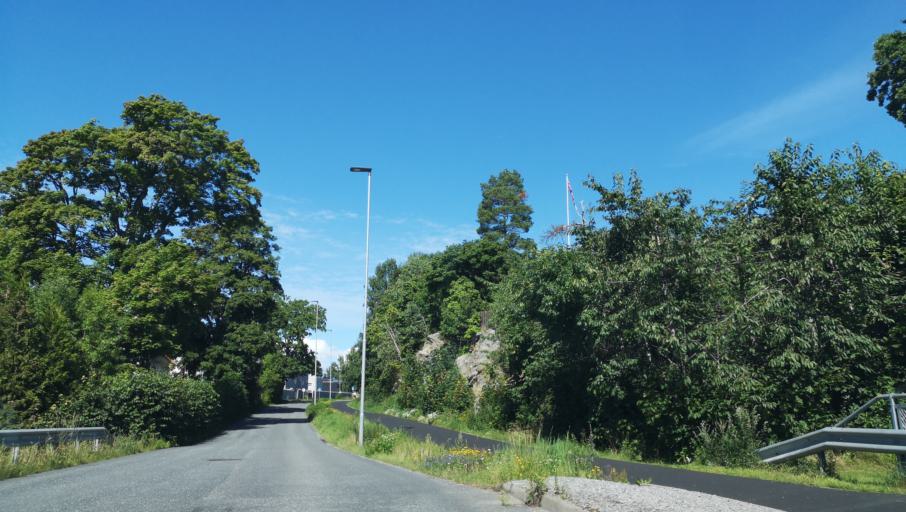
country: NO
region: Akershus
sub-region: Frogn
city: Drobak
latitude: 59.6574
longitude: 10.6416
